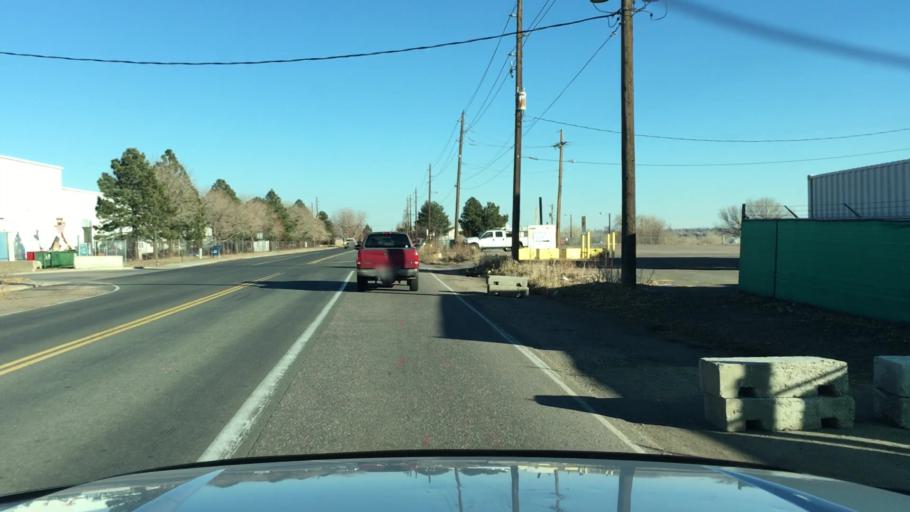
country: US
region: Colorado
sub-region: Jefferson County
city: Applewood
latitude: 39.7761
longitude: -105.1686
